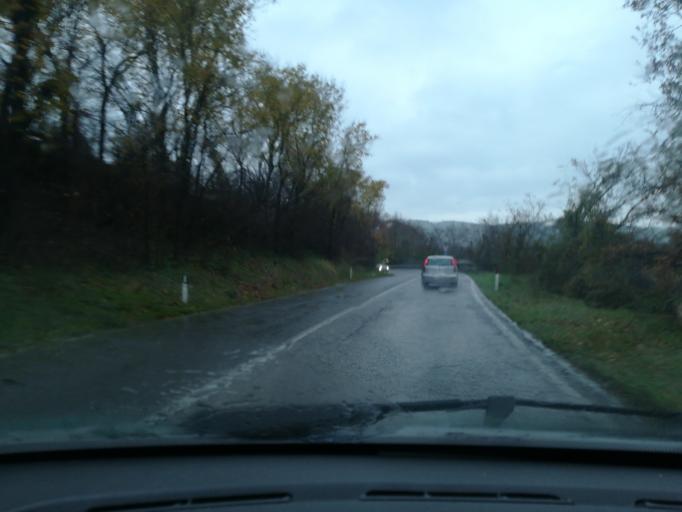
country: IT
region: The Marches
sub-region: Provincia di Macerata
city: Sforzacosta
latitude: 43.2620
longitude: 13.4215
